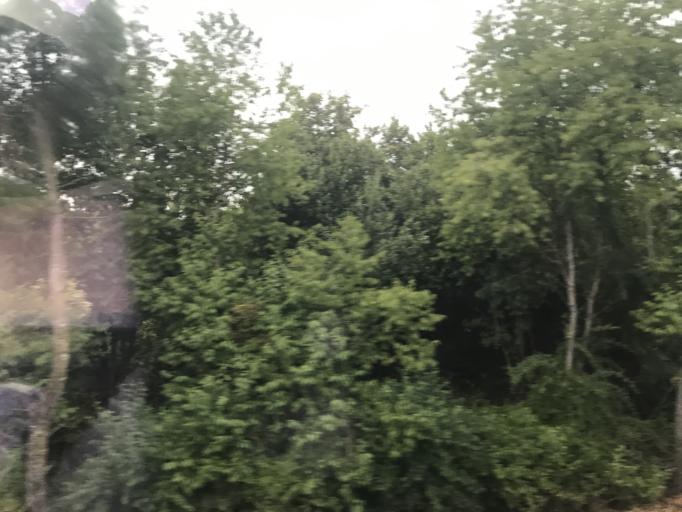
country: DE
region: Bavaria
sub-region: Regierungsbezirk Unterfranken
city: Bergtheim
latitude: 49.9107
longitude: 10.0829
